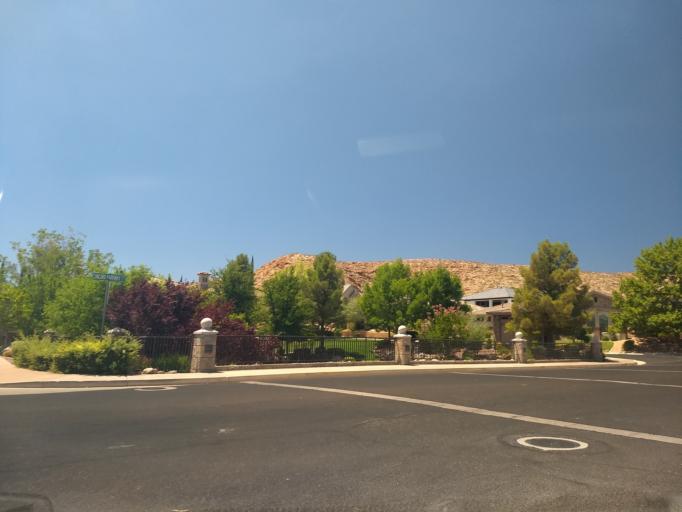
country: US
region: Utah
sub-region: Washington County
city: Washington
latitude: 37.1493
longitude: -113.5296
